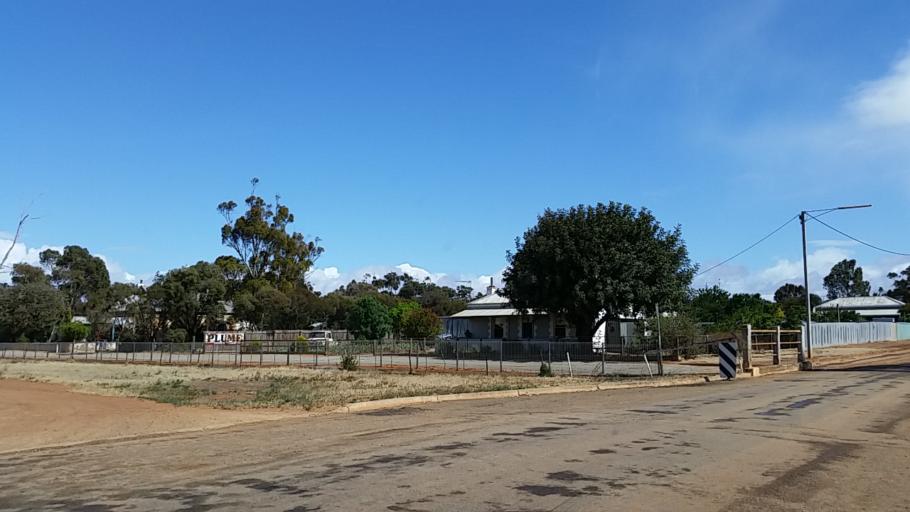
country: AU
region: South Australia
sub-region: Peterborough
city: Peterborough
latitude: -32.9712
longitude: 138.8393
